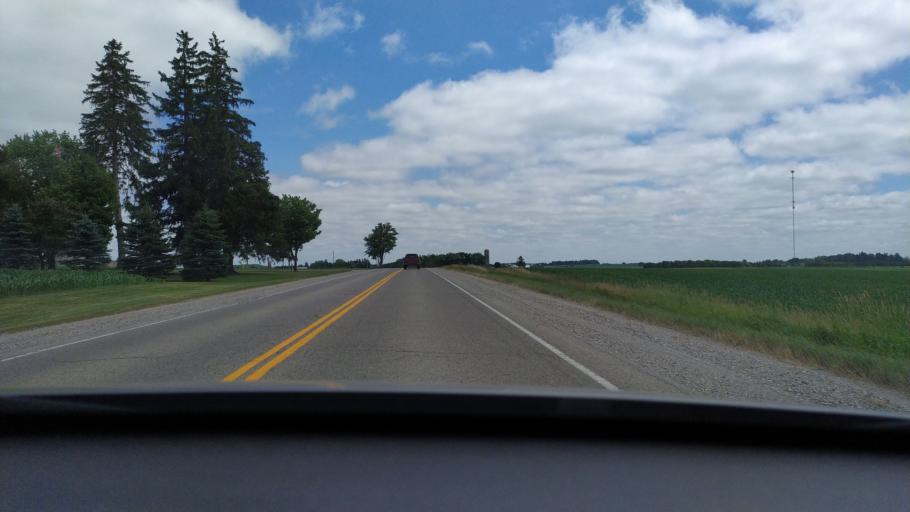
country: CA
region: Ontario
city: Stratford
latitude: 43.2916
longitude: -80.9707
